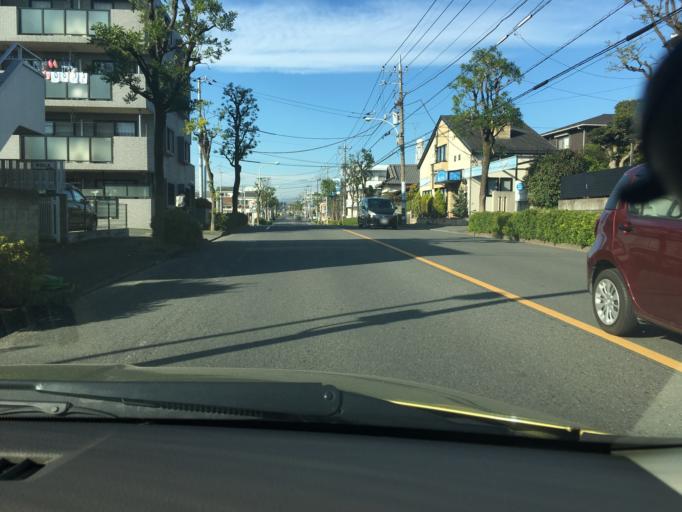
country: JP
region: Tokyo
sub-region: Machida-shi
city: Machida
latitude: 35.5658
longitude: 139.4193
